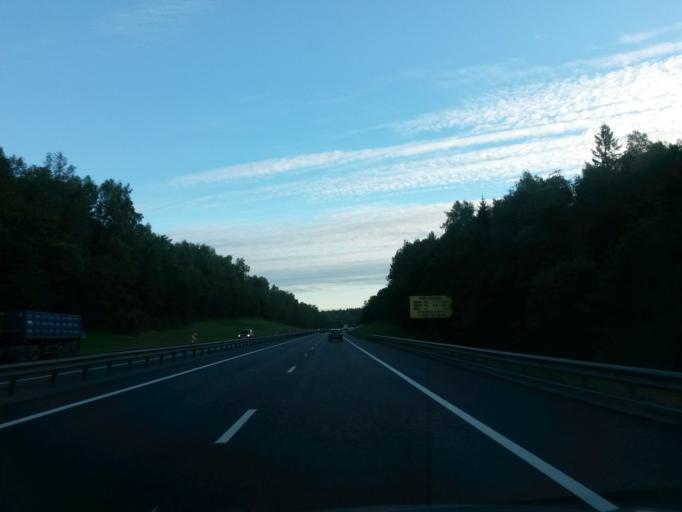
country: RU
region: Moskovskaya
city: Krasnozavodsk
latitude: 56.4483
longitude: 38.3466
